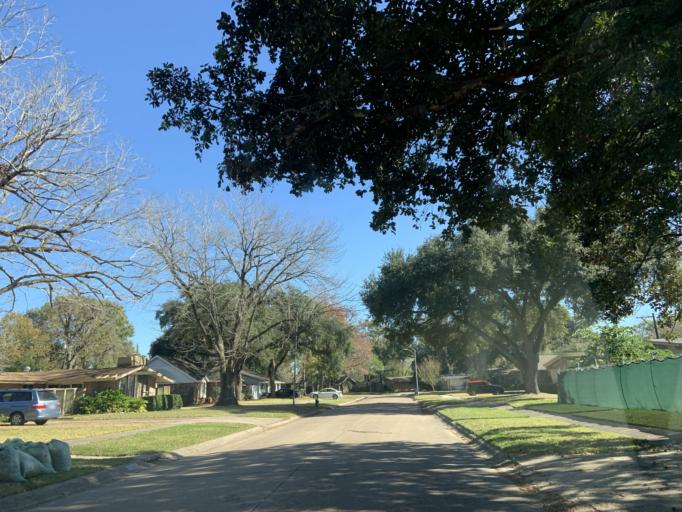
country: US
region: Texas
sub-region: Harris County
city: Bellaire
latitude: 29.6801
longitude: -95.5004
